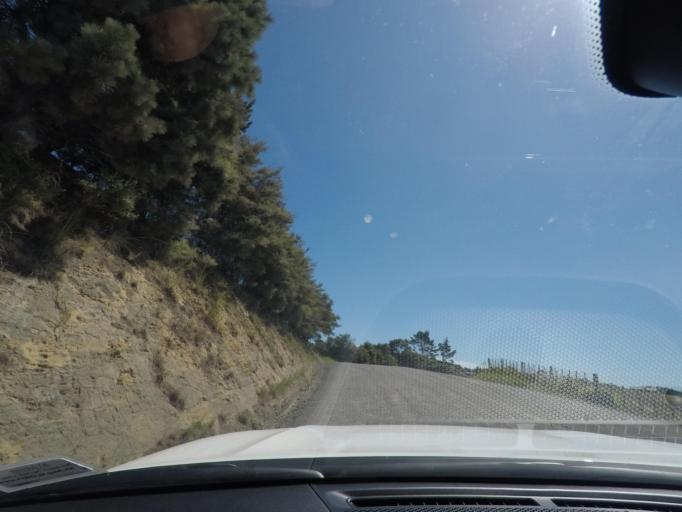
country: NZ
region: Auckland
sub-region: Auckland
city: Parakai
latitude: -36.5818
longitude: 174.3106
